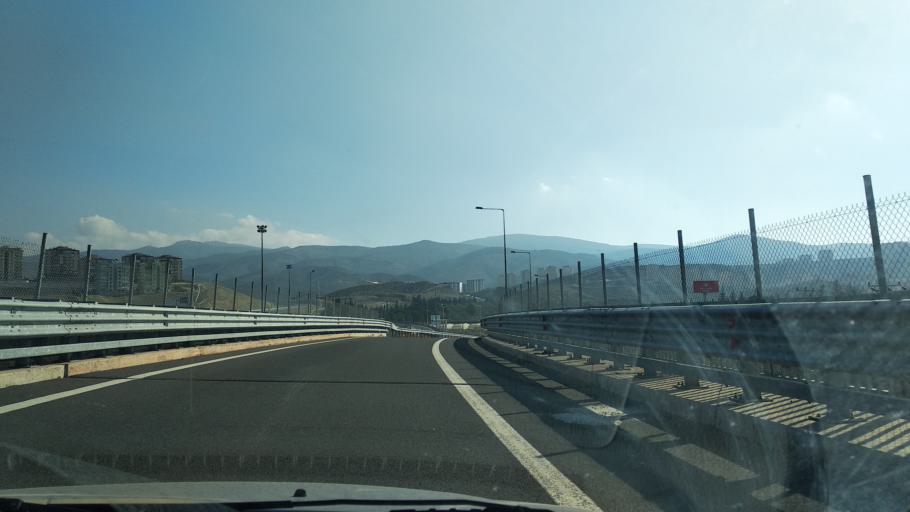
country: TR
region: Izmir
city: Menemen
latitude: 38.5709
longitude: 27.0536
